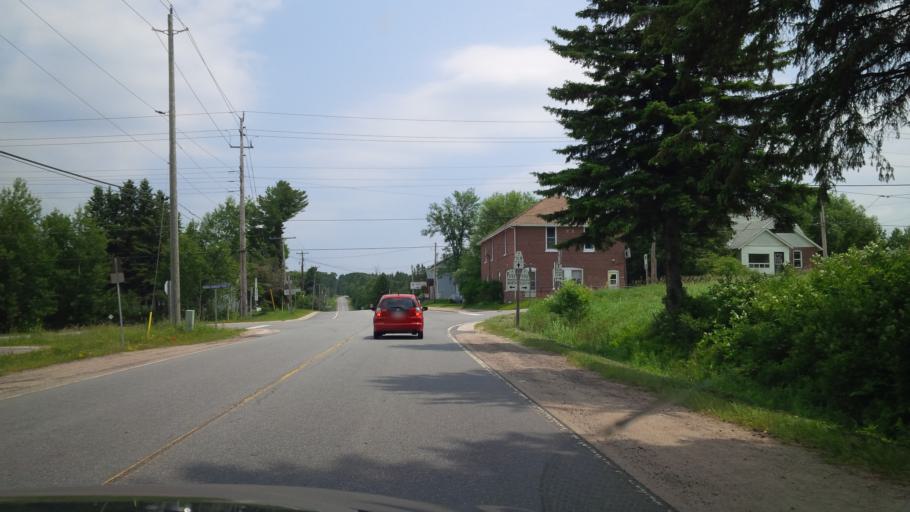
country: CA
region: Ontario
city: Huntsville
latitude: 45.5289
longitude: -79.3173
